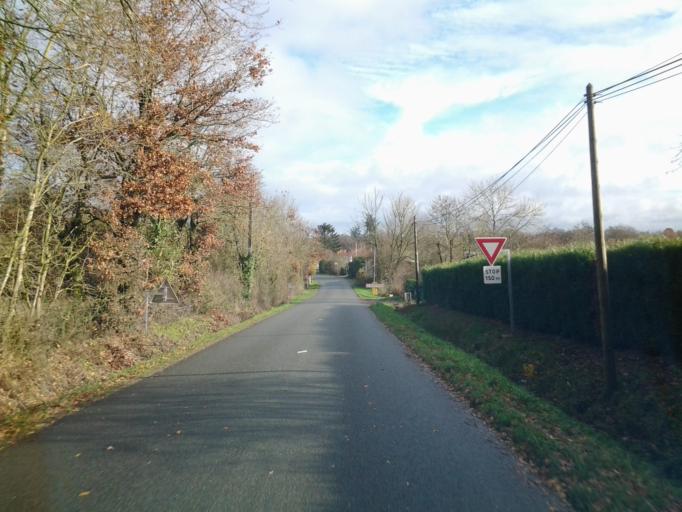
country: FR
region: Pays de la Loire
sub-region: Departement de la Vendee
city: Saint-Florent-des-Bois
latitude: 46.6282
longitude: -1.3138
